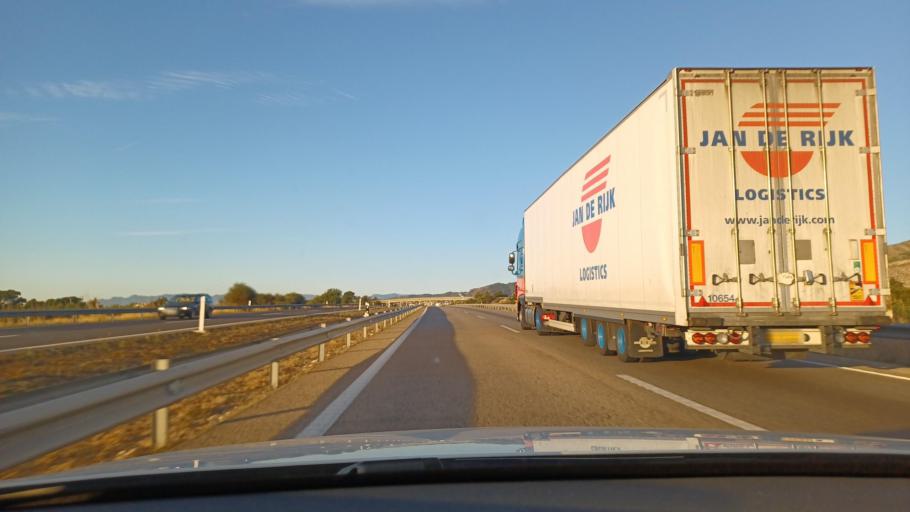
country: ES
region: Valencia
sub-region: Provincia de Castello
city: Castello de la Plana
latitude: 40.0317
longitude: -0.0022
